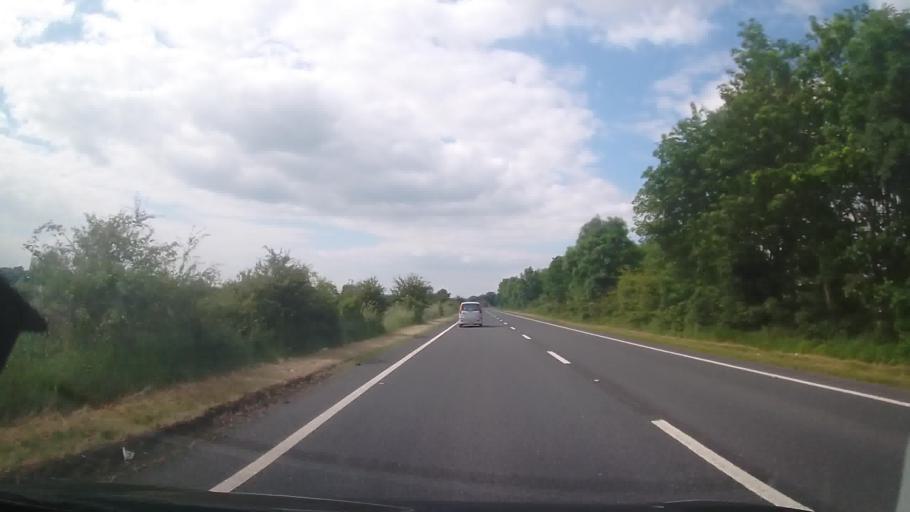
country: GB
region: England
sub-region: Herefordshire
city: Leominster
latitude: 52.2137
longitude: -2.7248
